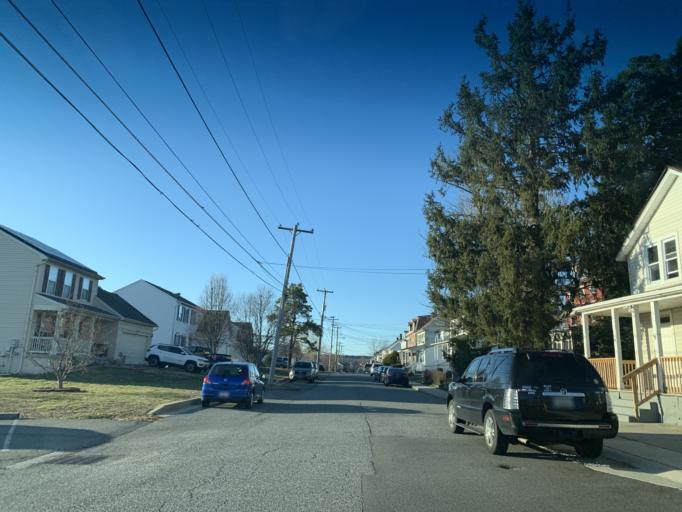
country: US
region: Maryland
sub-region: Cecil County
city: Perryville
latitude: 39.5593
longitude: -76.0775
